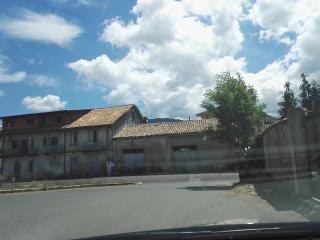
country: IT
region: Calabria
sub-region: Provincia di Vibo-Valentia
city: Serra San Bruno
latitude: 38.5754
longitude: 16.3214
